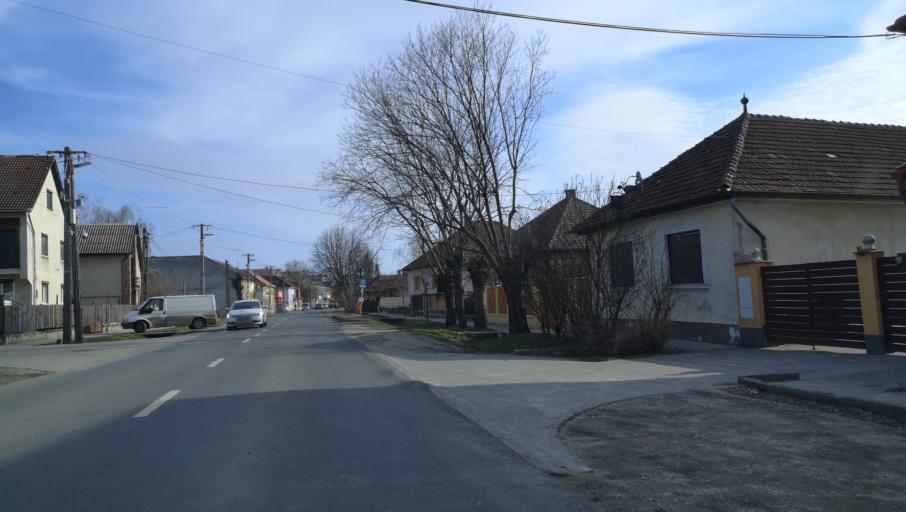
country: HU
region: Pest
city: Monor
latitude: 47.3546
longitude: 19.4428
